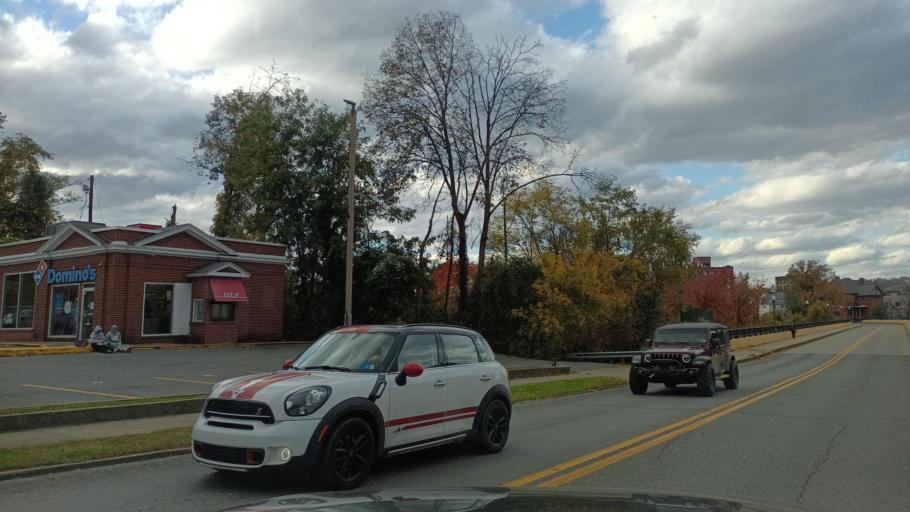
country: US
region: West Virginia
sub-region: Monongalia County
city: Morgantown
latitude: 39.6262
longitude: -79.9550
